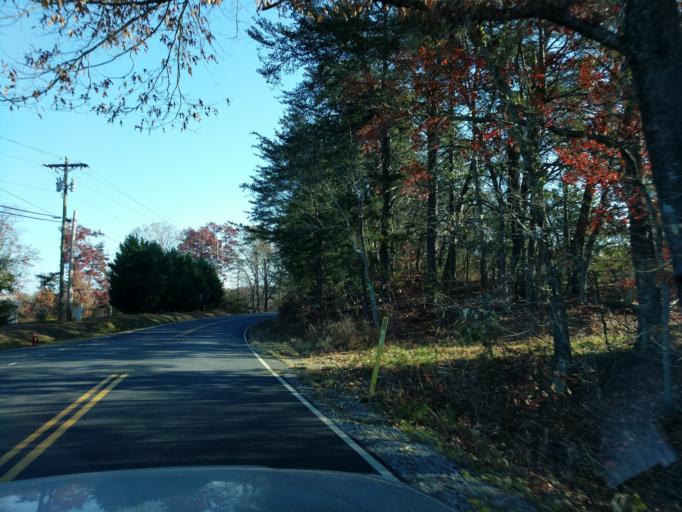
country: US
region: North Carolina
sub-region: Polk County
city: Columbus
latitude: 35.2529
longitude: -82.0812
